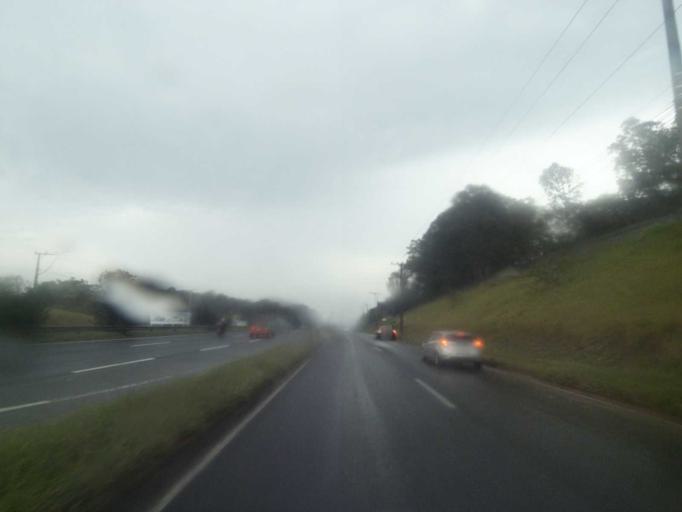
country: BR
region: Rio Grande do Sul
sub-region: Sapucaia Do Sul
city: Sapucaia
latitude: -29.7971
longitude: -51.1652
